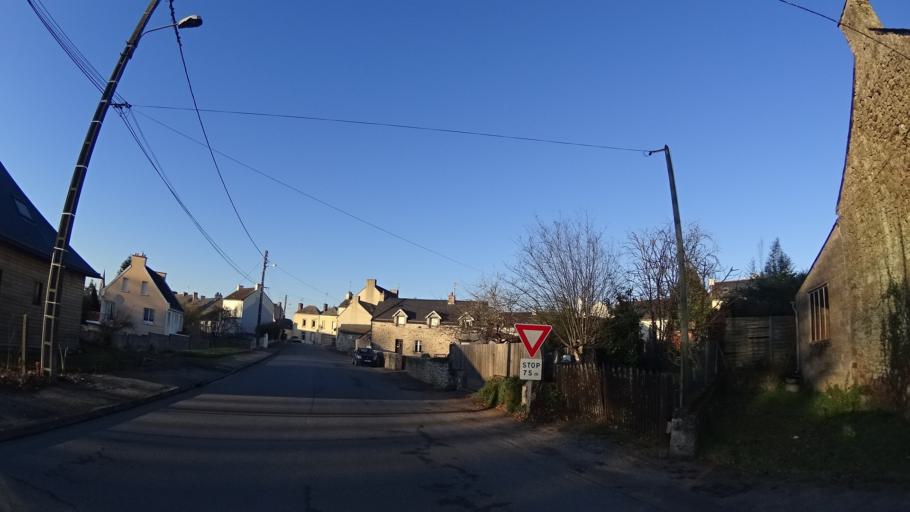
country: FR
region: Brittany
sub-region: Departement du Morbihan
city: Saint-Jean-la-Poterie
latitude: 47.6349
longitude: -2.1214
